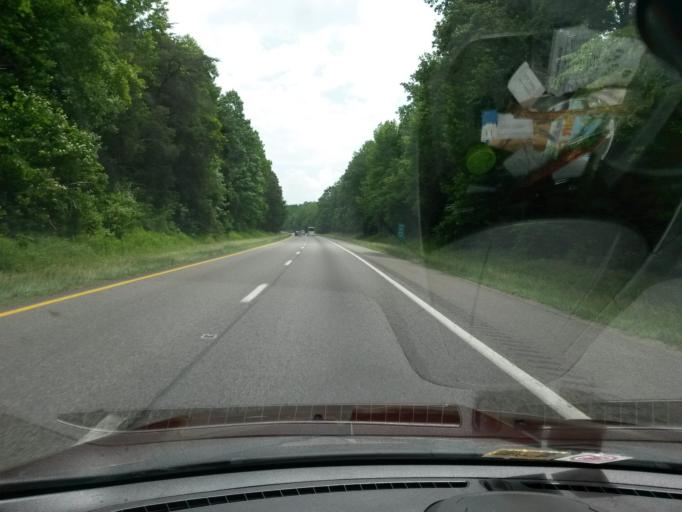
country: US
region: Virginia
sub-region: Goochland County
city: Goochland
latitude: 37.7213
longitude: -77.8153
